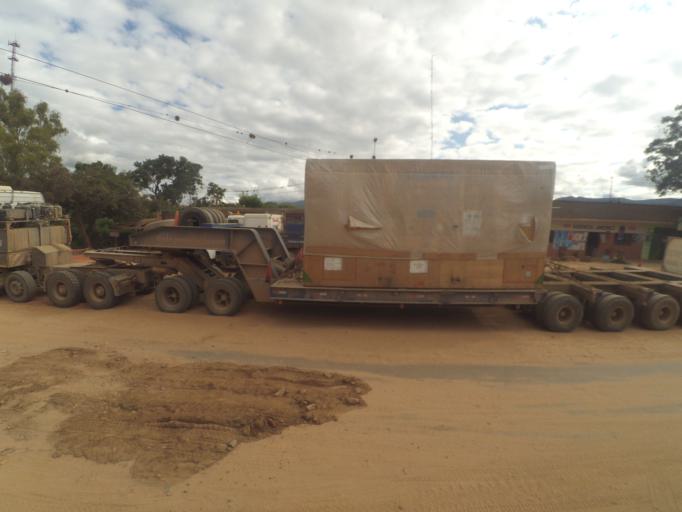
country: BO
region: Santa Cruz
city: Samaipata
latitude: -18.1637
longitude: -63.9236
